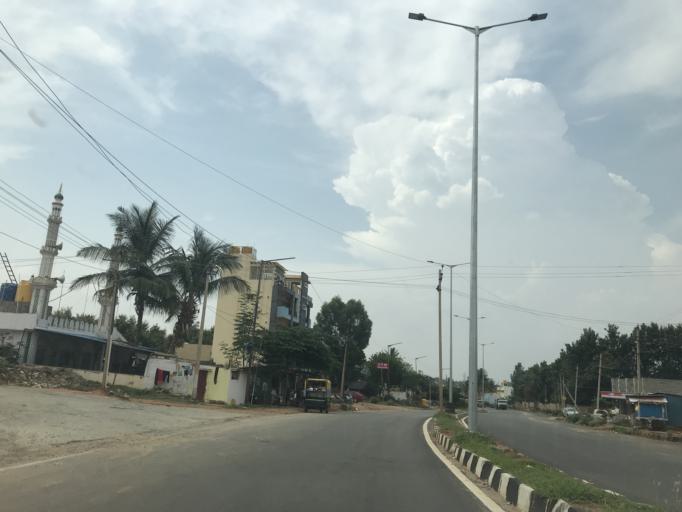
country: IN
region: Karnataka
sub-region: Bangalore Urban
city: Yelahanka
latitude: 13.1306
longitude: 77.6665
